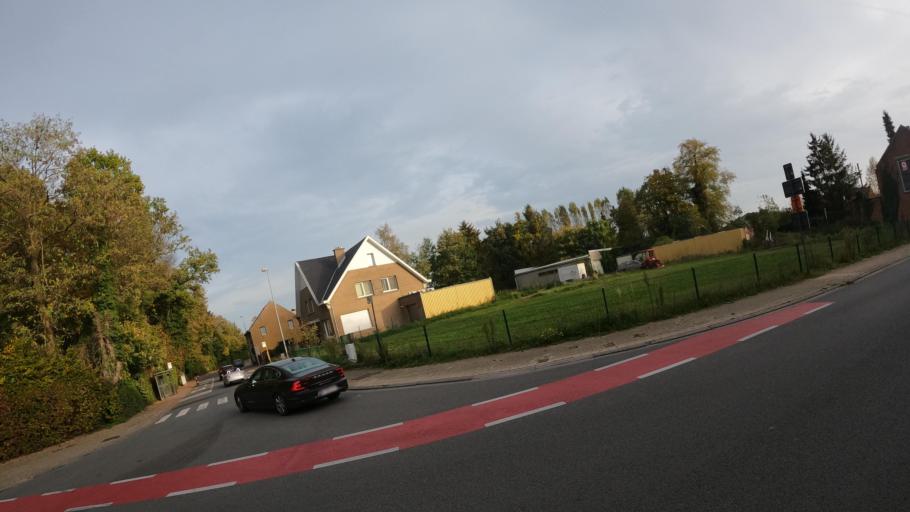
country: BE
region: Flanders
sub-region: Provincie Oost-Vlaanderen
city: Sint-Niklaas
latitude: 51.1490
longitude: 4.1322
